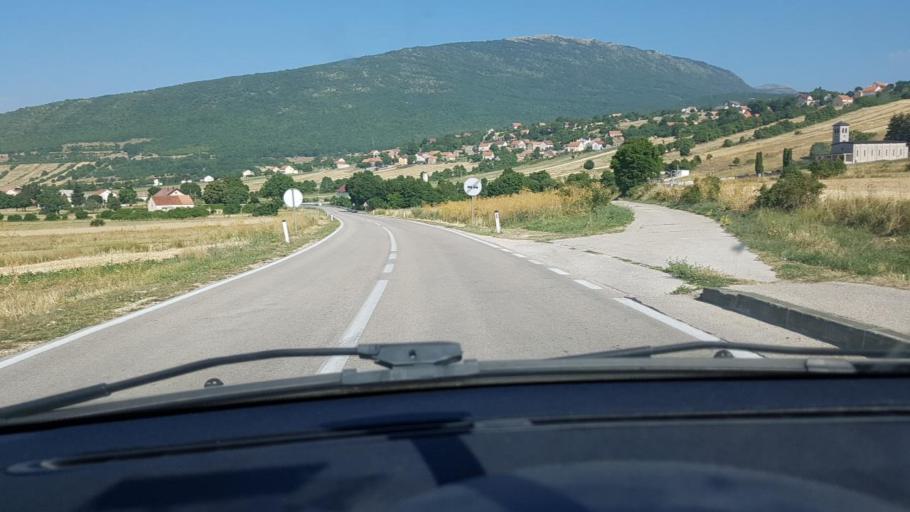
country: BA
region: Federation of Bosnia and Herzegovina
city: Zabrisce
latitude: 43.8692
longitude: 16.9255
